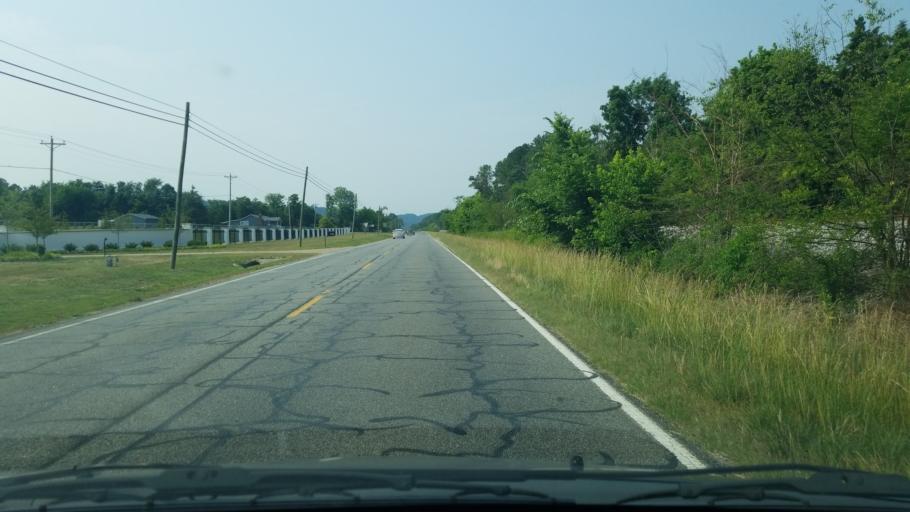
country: US
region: Georgia
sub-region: Catoosa County
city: Ringgold
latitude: 34.9527
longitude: -85.1041
